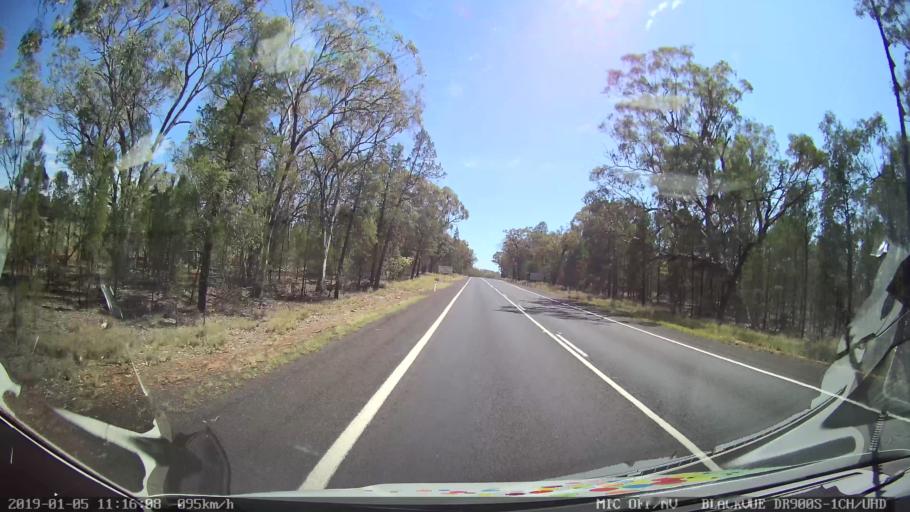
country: AU
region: New South Wales
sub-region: Warrumbungle Shire
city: Coonabarabran
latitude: -31.3430
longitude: 149.2968
